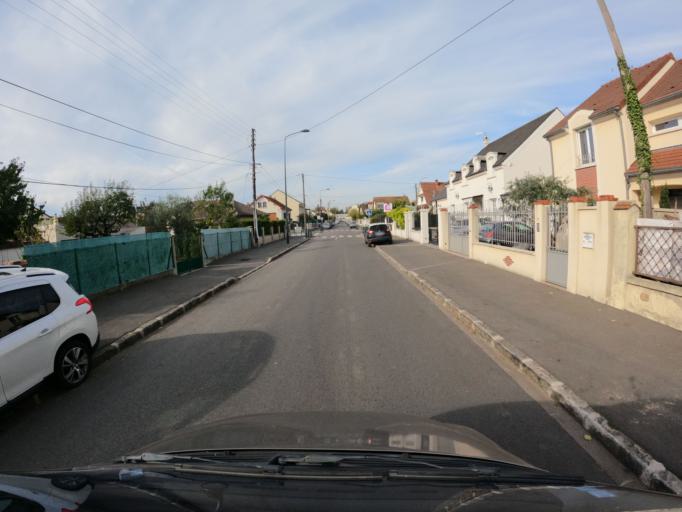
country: FR
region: Ile-de-France
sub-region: Departement de Seine-et-Marne
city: Pontault-Combault
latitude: 48.7963
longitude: 2.6068
